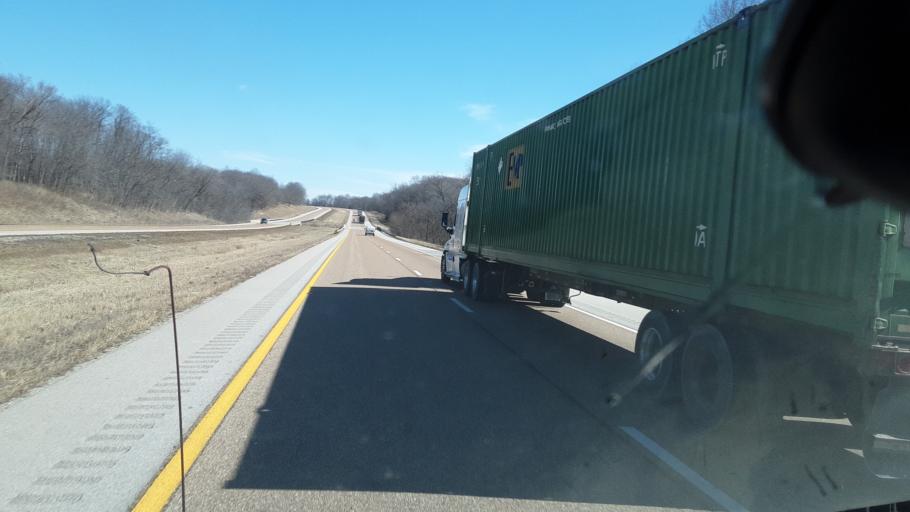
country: US
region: Illinois
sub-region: Clark County
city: Casey
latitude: 39.2823
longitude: -88.0660
